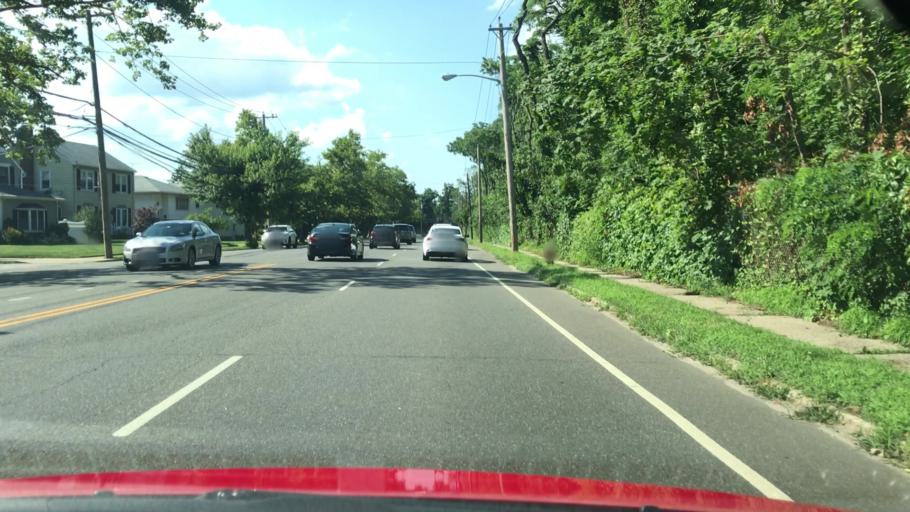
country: US
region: New York
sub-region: Nassau County
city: Malverne
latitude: 40.6740
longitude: -73.6630
